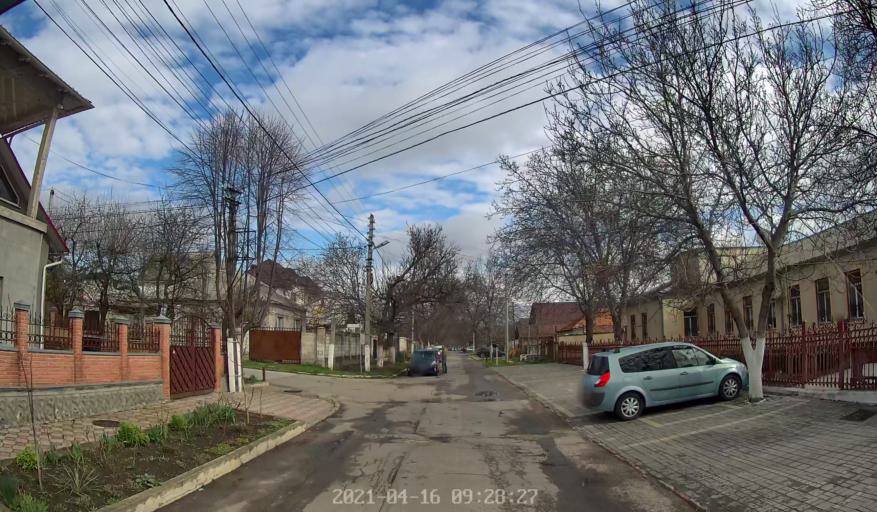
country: MD
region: Chisinau
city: Stauceni
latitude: 47.0534
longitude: 28.8454
